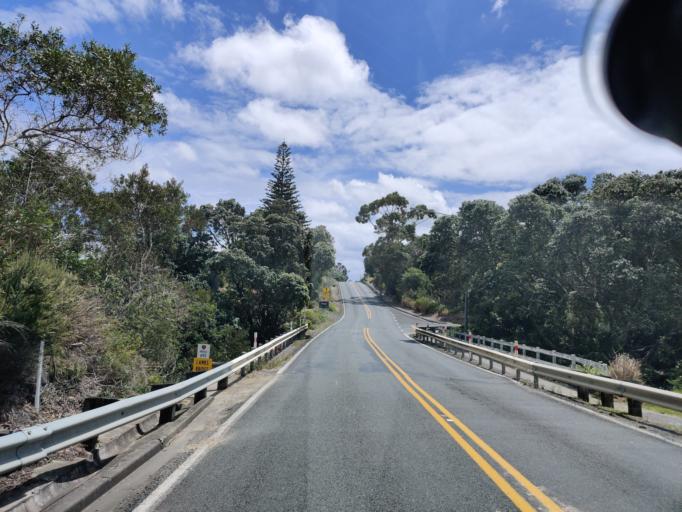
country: NZ
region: Northland
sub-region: Far North District
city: Kaitaia
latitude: -34.8114
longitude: 173.1163
